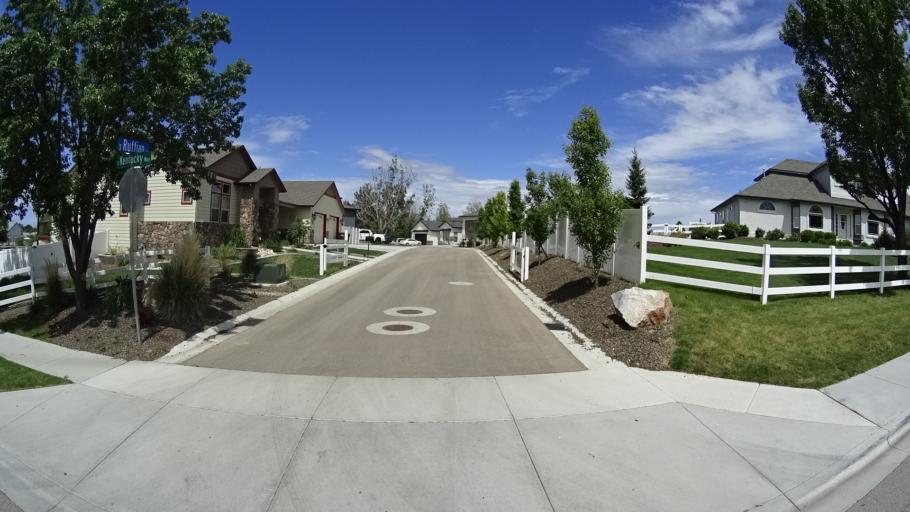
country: US
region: Idaho
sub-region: Ada County
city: Meridian
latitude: 43.5743
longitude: -116.4048
